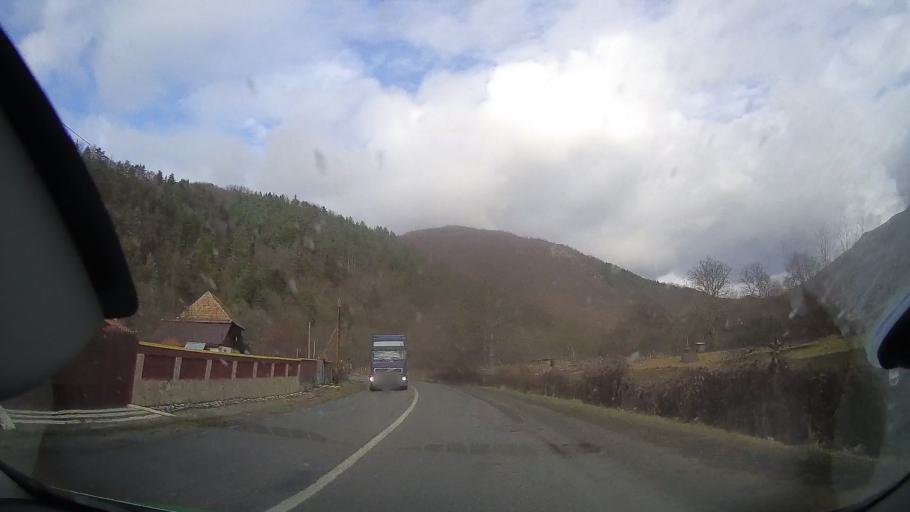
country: RO
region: Alba
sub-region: Comuna Ocolis
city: Ocolis
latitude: 46.4786
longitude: 23.5077
